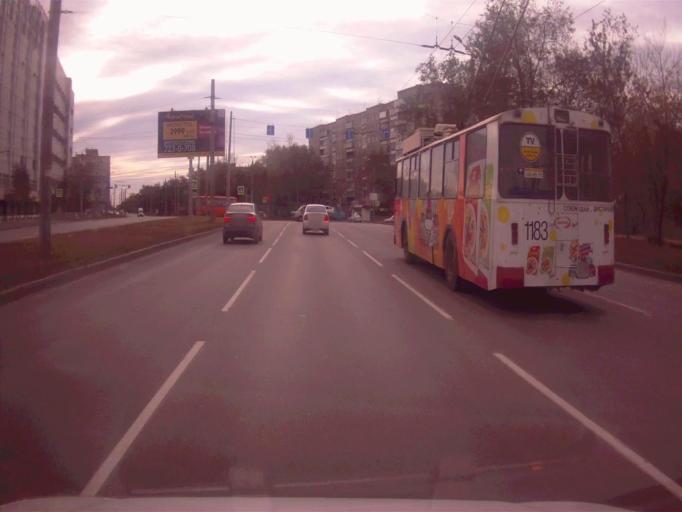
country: RU
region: Chelyabinsk
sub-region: Gorod Chelyabinsk
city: Chelyabinsk
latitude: 55.1260
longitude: 61.4767
